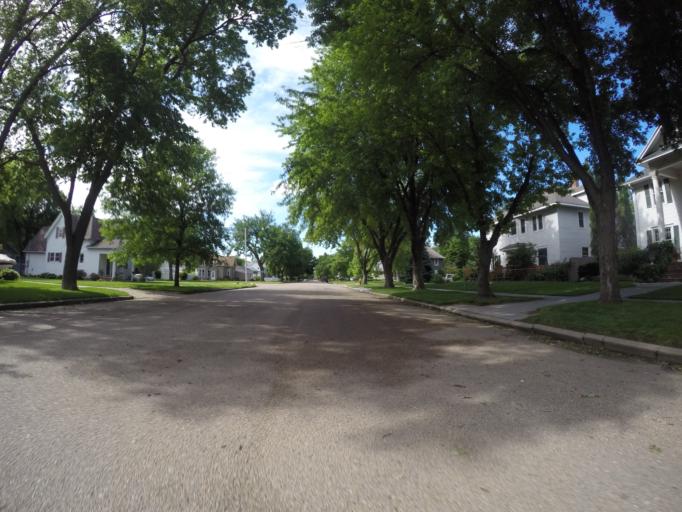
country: US
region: Nebraska
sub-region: Buffalo County
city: Kearney
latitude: 40.6993
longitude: -99.0899
